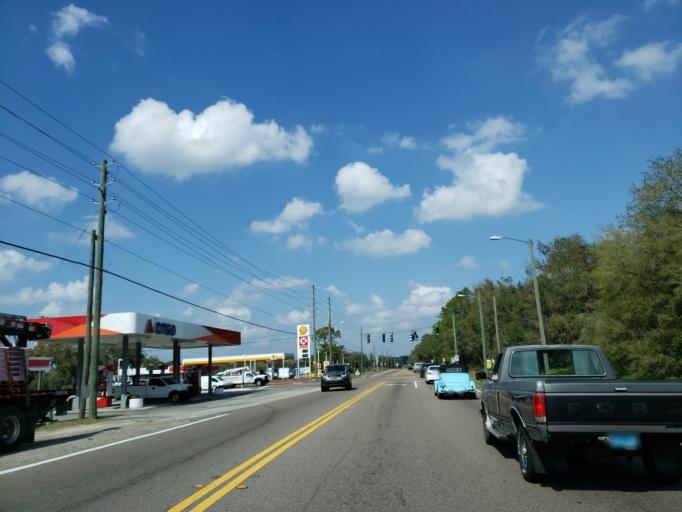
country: US
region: Florida
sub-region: Hillsborough County
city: Keystone
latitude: 28.1489
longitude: -82.5794
